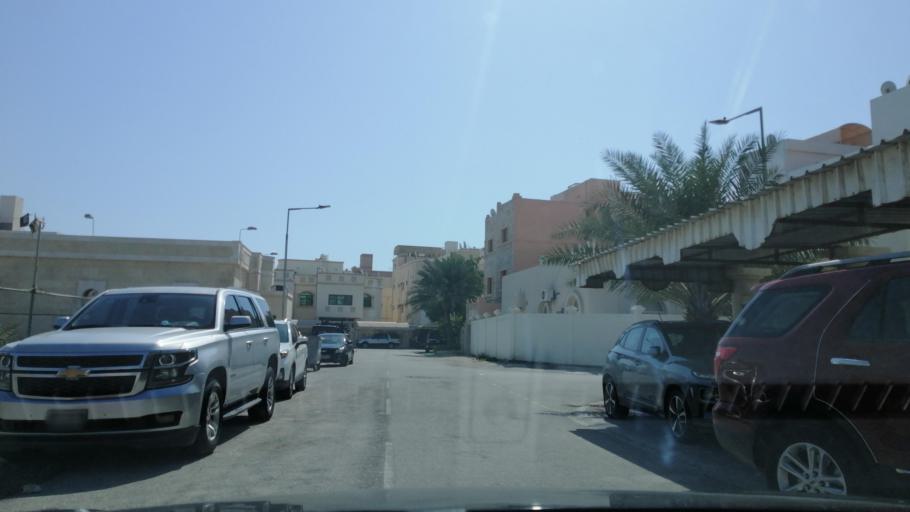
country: BH
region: Muharraq
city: Al Hadd
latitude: 26.2471
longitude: 50.6347
